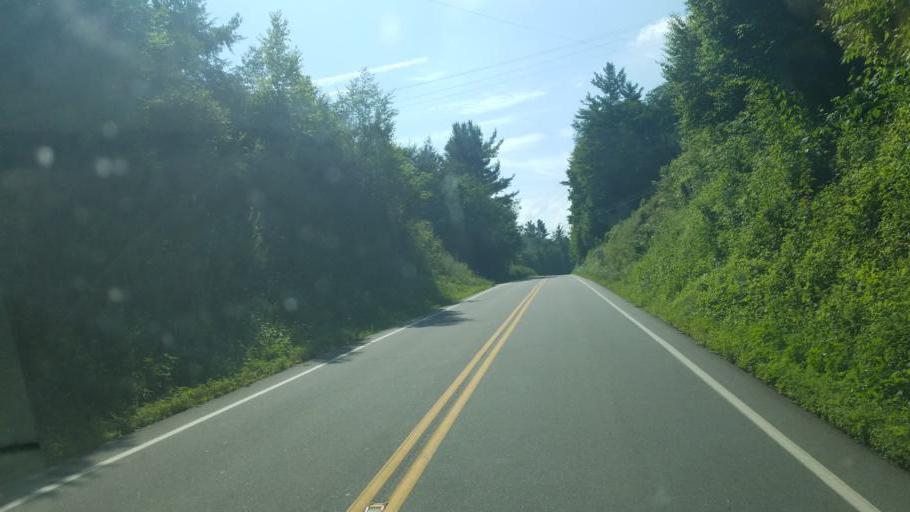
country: US
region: North Carolina
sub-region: Avery County
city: Newland
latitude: 36.0344
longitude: -81.9083
